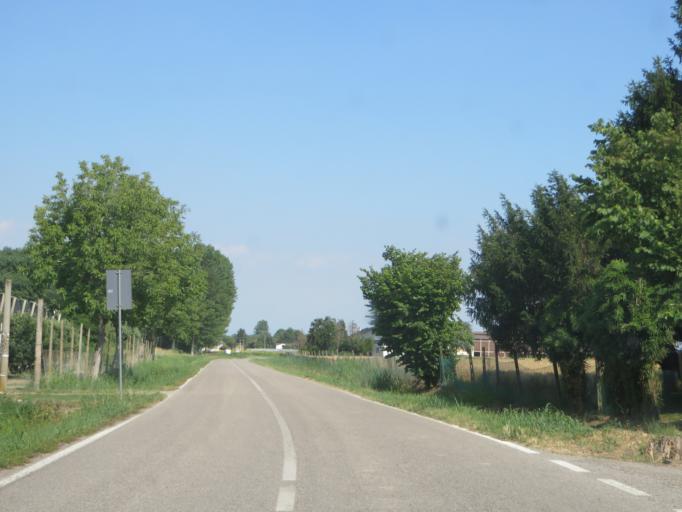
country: IT
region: Veneto
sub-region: Provincia di Verona
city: Angiari
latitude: 45.2254
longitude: 11.2624
